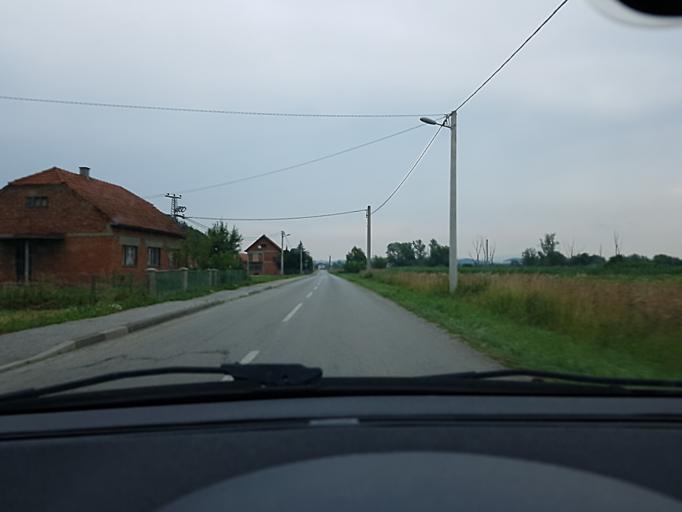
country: HR
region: Zagrebacka
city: Jakovlje
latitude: 45.9851
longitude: 15.8403
